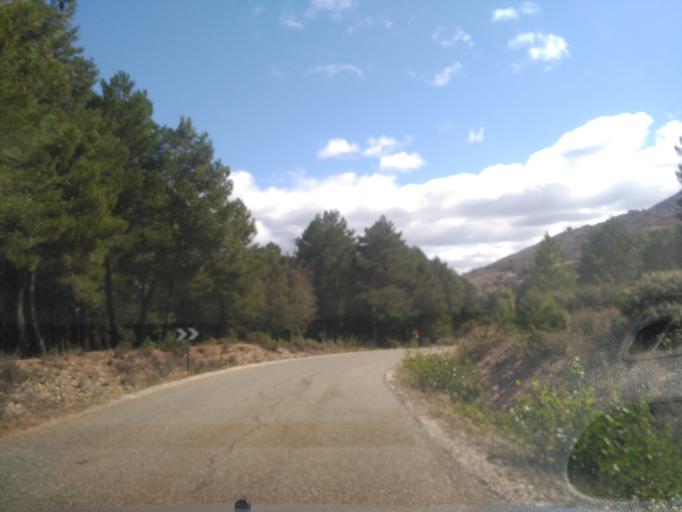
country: ES
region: Castille and Leon
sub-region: Provincia de Soria
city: Espejon
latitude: 41.8469
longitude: -3.2336
